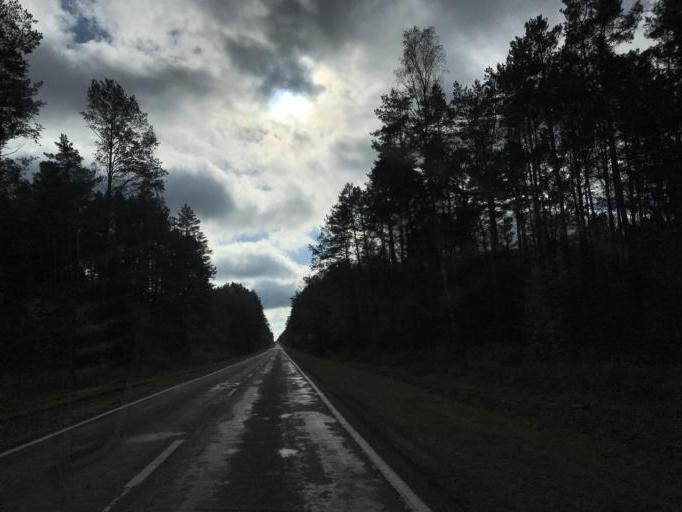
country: BY
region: Gomel
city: Dowsk
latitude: 53.3196
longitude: 30.4046
